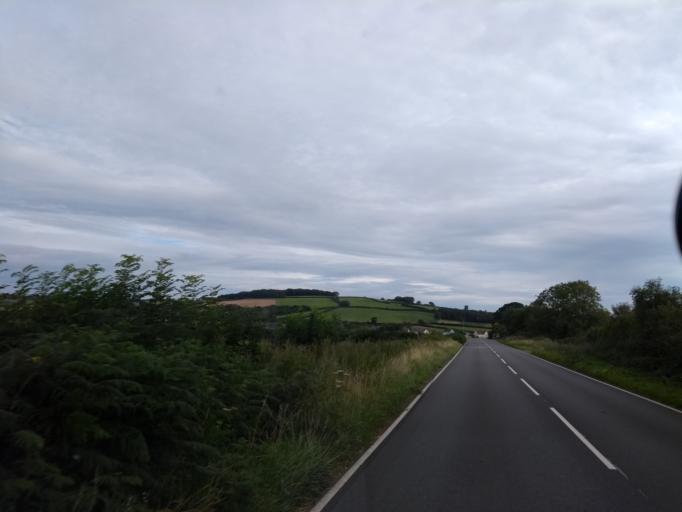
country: GB
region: England
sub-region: Dorset
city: Beaminster
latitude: 50.8376
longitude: -2.7771
